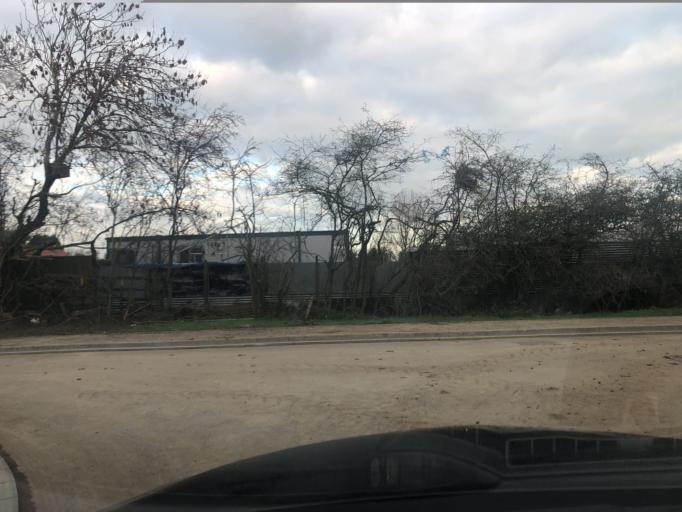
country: GB
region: England
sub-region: North Yorkshire
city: Northallerton
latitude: 54.3536
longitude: -1.4474
